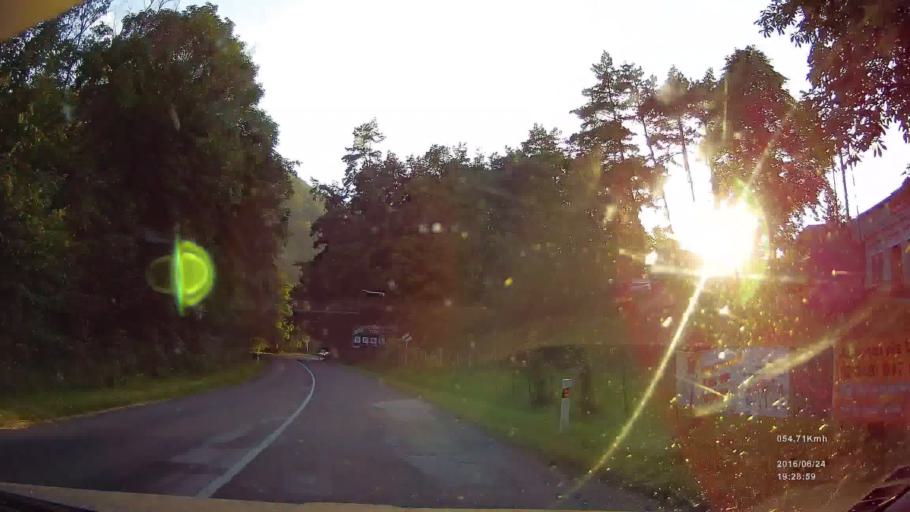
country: SK
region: Banskobystricky
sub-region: Okres Banska Bystrica
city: Brezno
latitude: 48.8062
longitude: 19.5498
